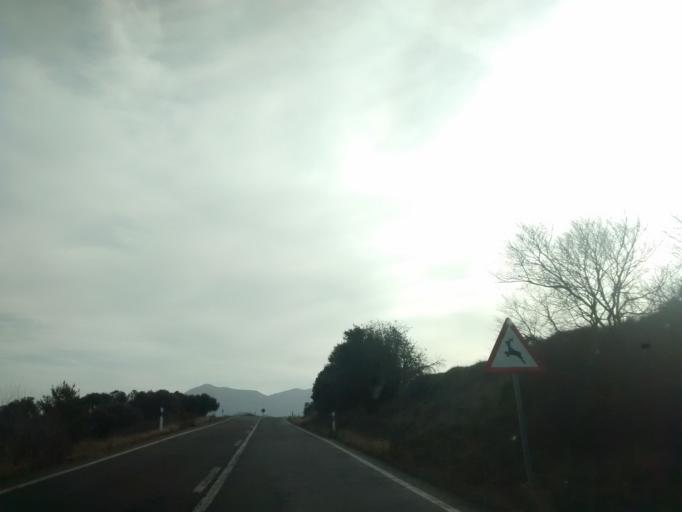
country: ES
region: Aragon
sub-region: Provincia de Huesca
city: Bailo
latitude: 42.5812
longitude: -0.8279
